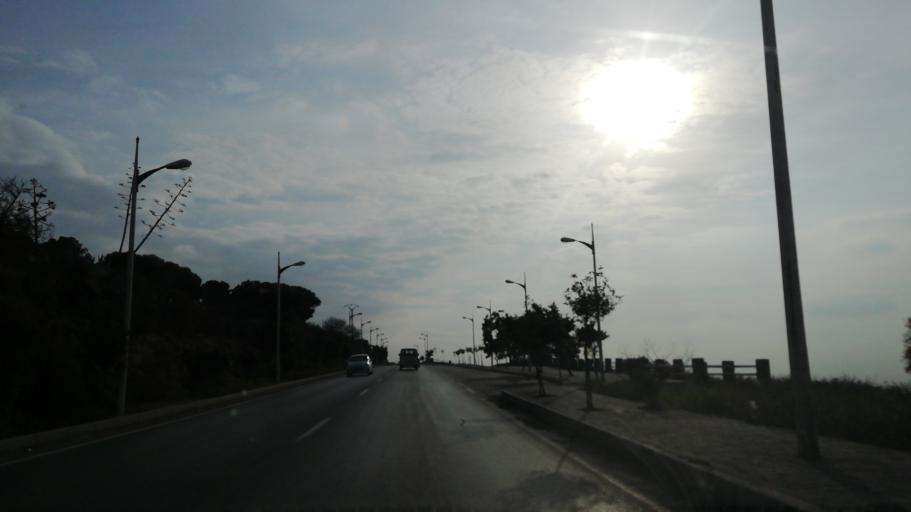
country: DZ
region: Mostaganem
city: Mostaganem
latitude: 35.9089
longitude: 0.0784
